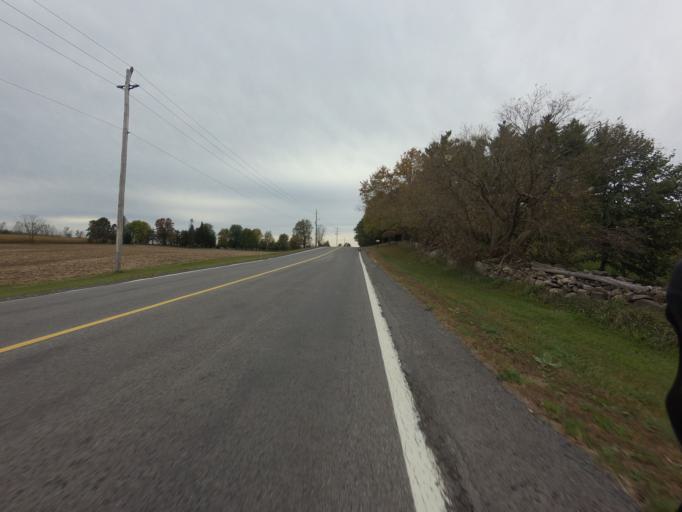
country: CA
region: Ontario
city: Bells Corners
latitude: 45.1125
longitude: -75.7266
